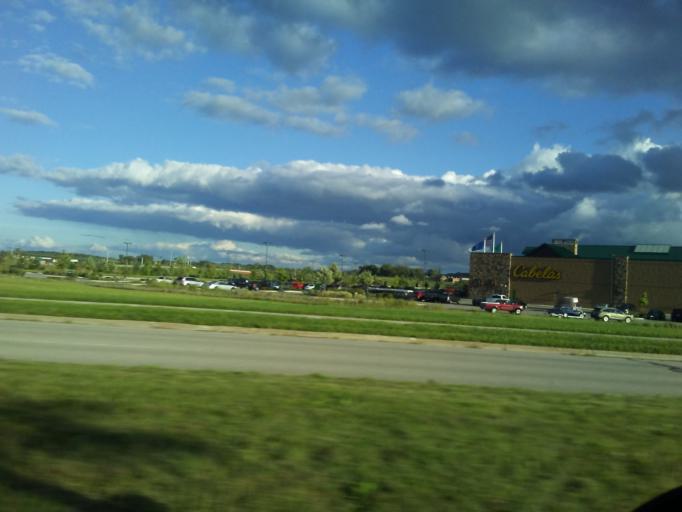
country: US
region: Wisconsin
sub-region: Dane County
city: Sun Prairie
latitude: 43.1656
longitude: -89.2734
